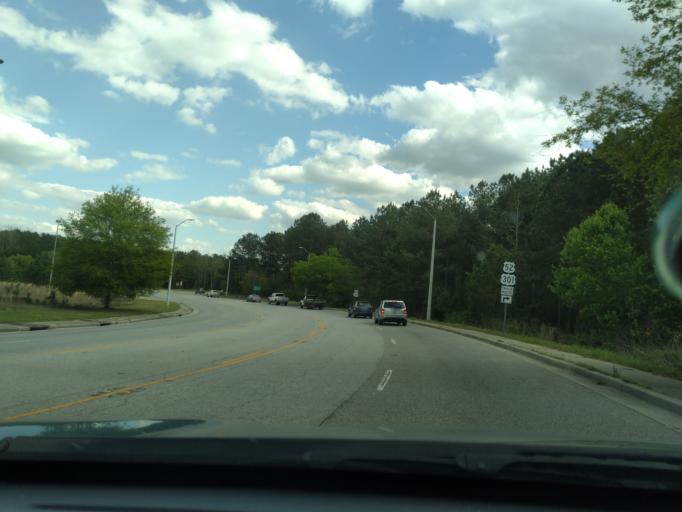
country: US
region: South Carolina
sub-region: Florence County
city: Florence
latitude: 34.1580
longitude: -79.7596
